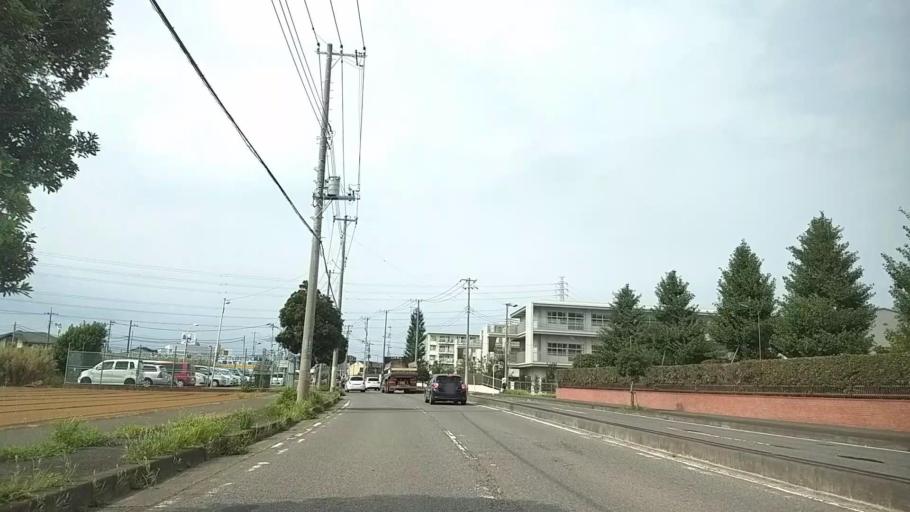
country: JP
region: Kanagawa
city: Atsugi
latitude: 35.4323
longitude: 139.3833
